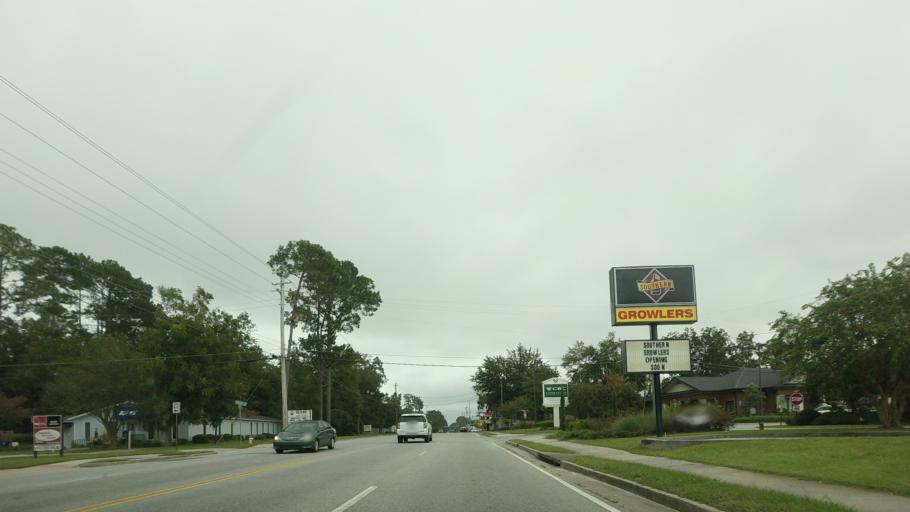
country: US
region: Georgia
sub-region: Lowndes County
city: Remerton
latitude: 30.8468
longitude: -83.3078
